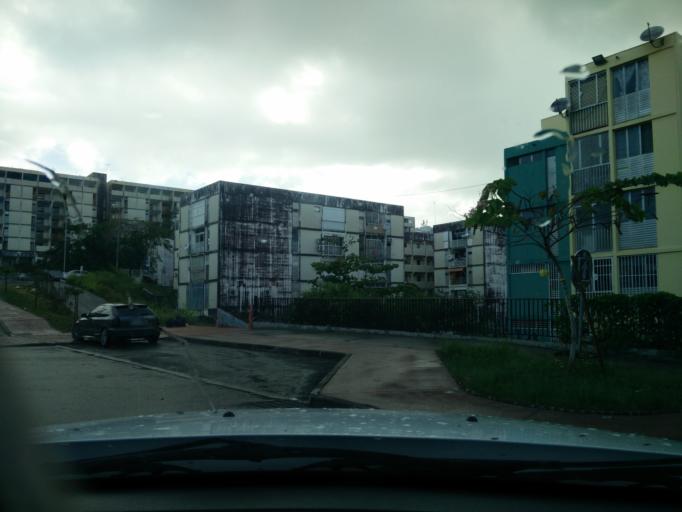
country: GP
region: Guadeloupe
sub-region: Guadeloupe
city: Pointe-a-Pitre
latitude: 16.2509
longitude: -61.5361
